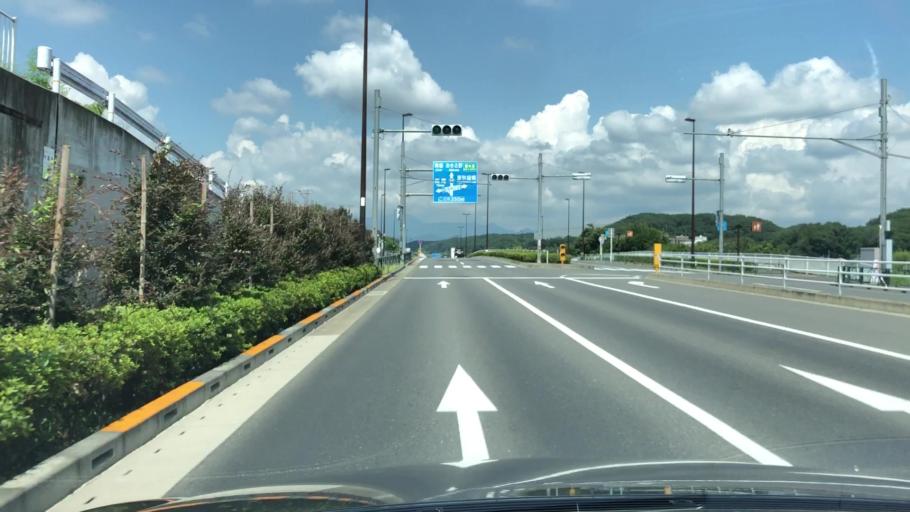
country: JP
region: Tokyo
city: Fussa
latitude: 35.7048
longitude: 139.3008
